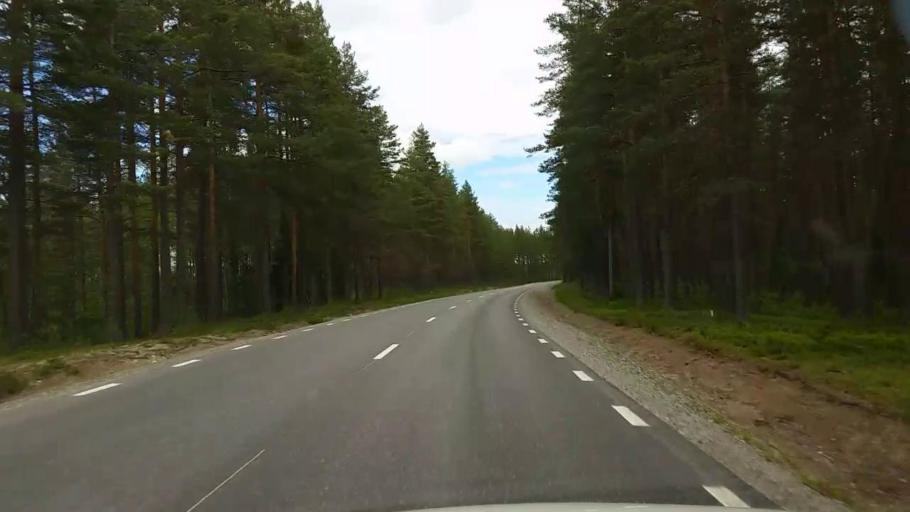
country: SE
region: Gaevleborg
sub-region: Sandvikens Kommun
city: Jarbo
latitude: 60.9499
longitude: 16.3939
